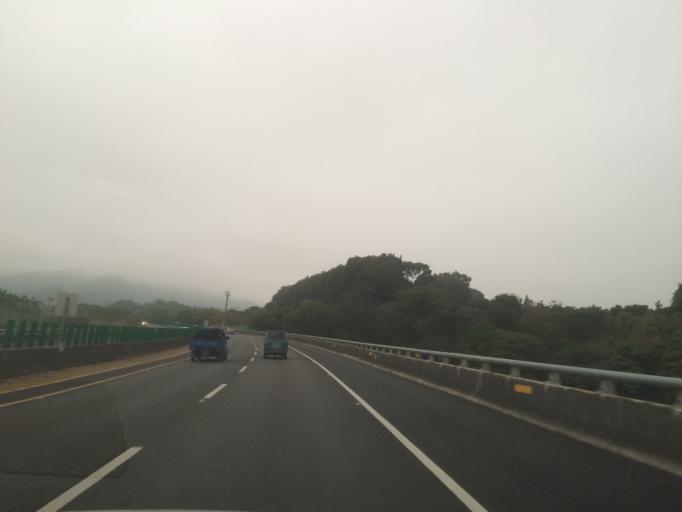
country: TW
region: Taiwan
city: Zhongxing New Village
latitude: 23.9884
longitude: 120.7824
